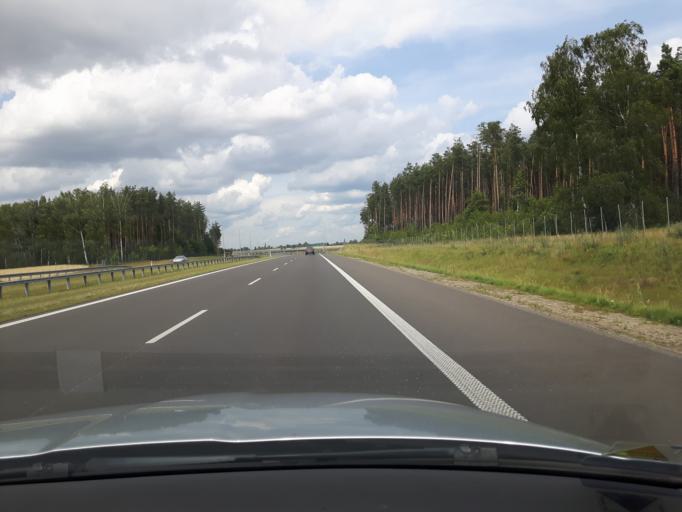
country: PL
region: Masovian Voivodeship
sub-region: Powiat mlawski
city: Wieczfnia Koscielna
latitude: 53.2699
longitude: 20.4332
